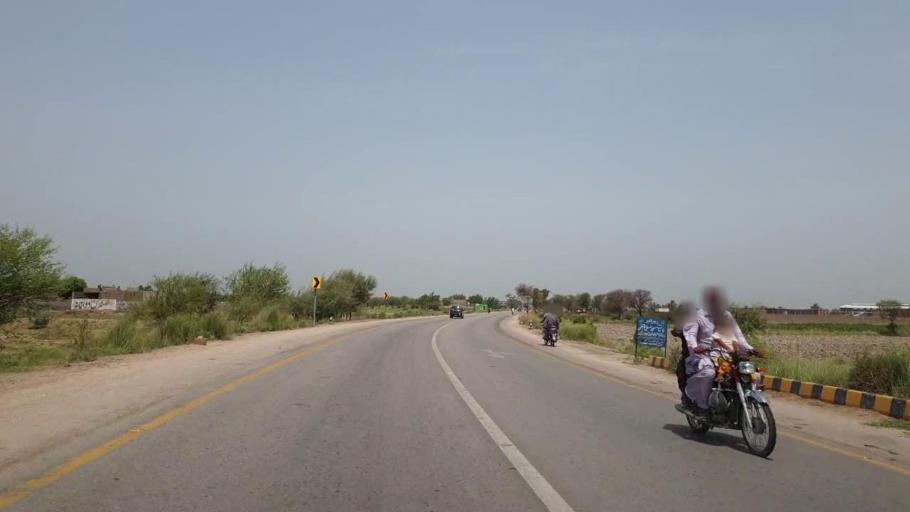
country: PK
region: Sindh
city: Nawabshah
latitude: 26.2144
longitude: 68.5093
